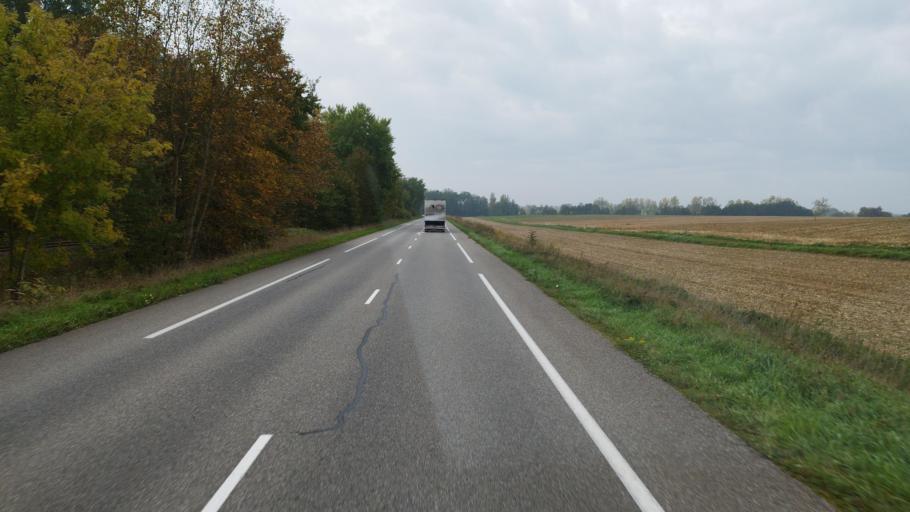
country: FR
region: Alsace
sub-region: Departement du Bas-Rhin
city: Wissembourg
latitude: 48.9741
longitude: 7.9544
